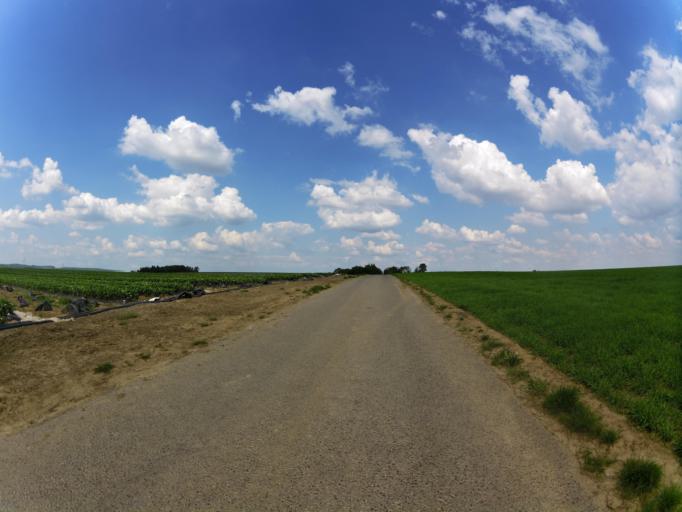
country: DE
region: Bavaria
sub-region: Regierungsbezirk Unterfranken
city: Sulzdorf
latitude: 49.6279
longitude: 9.9081
